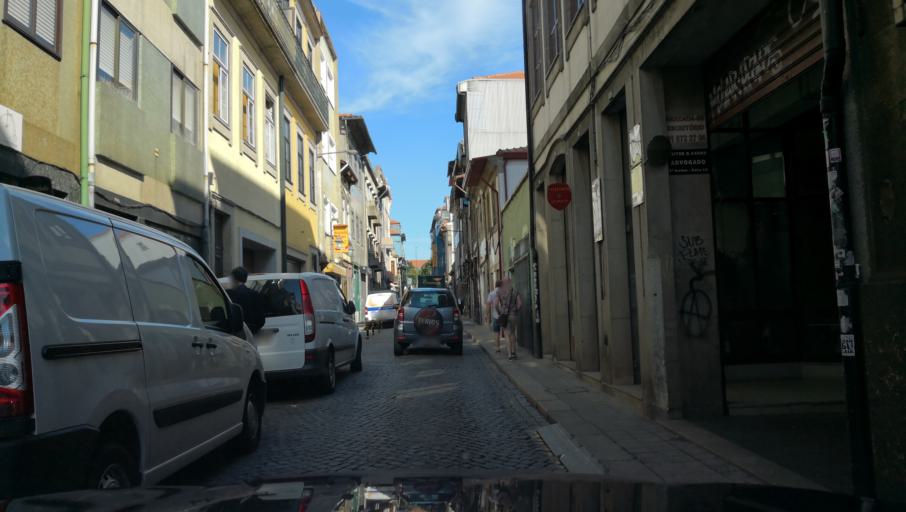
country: PT
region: Porto
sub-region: Porto
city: Porto
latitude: 41.1520
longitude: -8.6137
